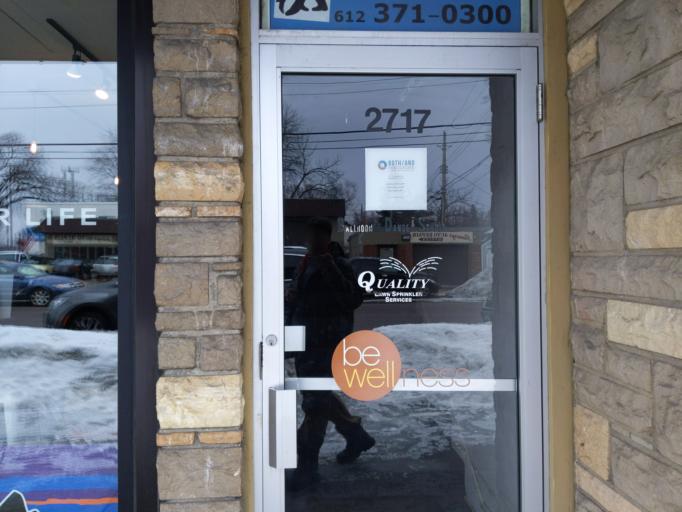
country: US
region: Minnesota
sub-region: Hennepin County
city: Minneapolis
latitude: 44.9268
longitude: -93.2327
